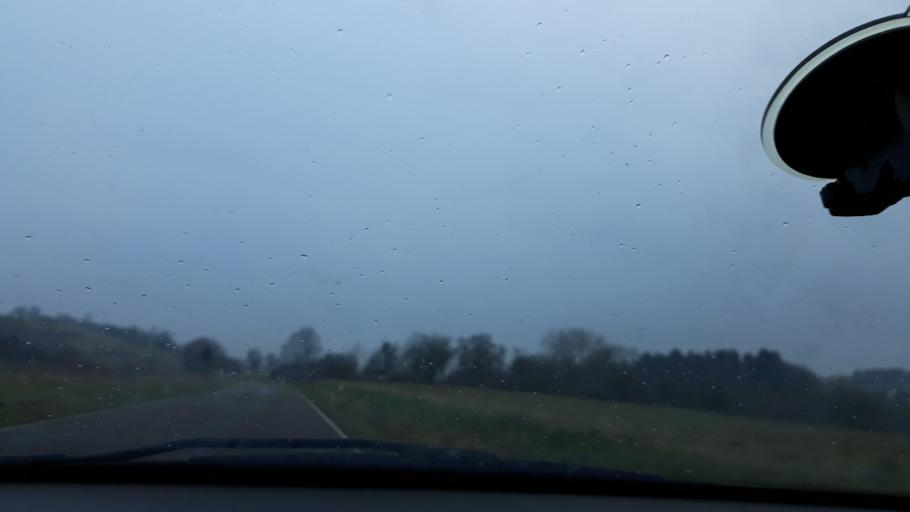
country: DE
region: Saarland
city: Blieskastel
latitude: 49.2110
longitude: 7.2368
